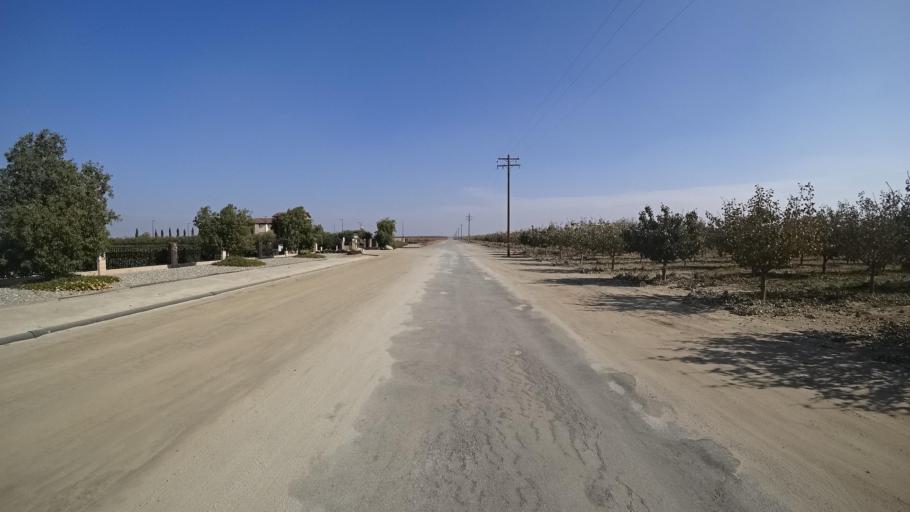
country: US
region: California
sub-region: Kern County
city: Shafter
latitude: 35.5440
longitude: -119.1492
